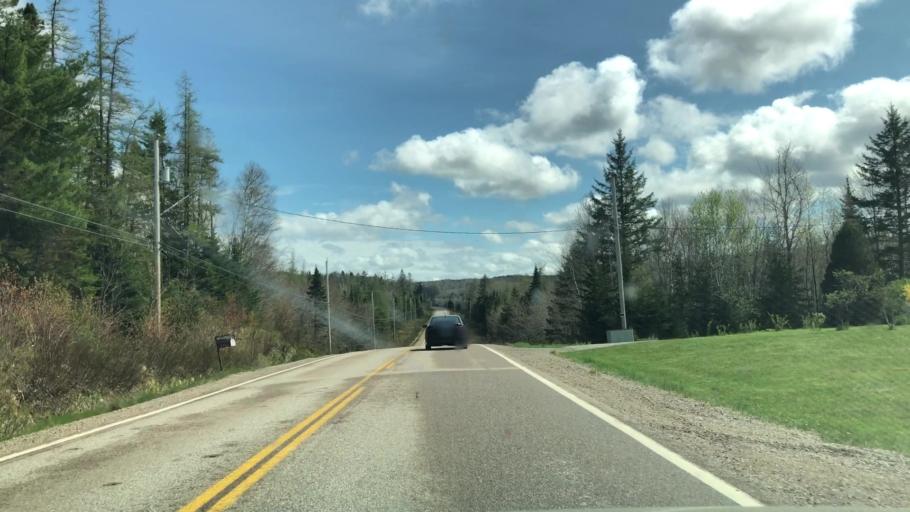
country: CA
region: Nova Scotia
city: Antigonish
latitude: 45.2072
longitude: -62.0038
